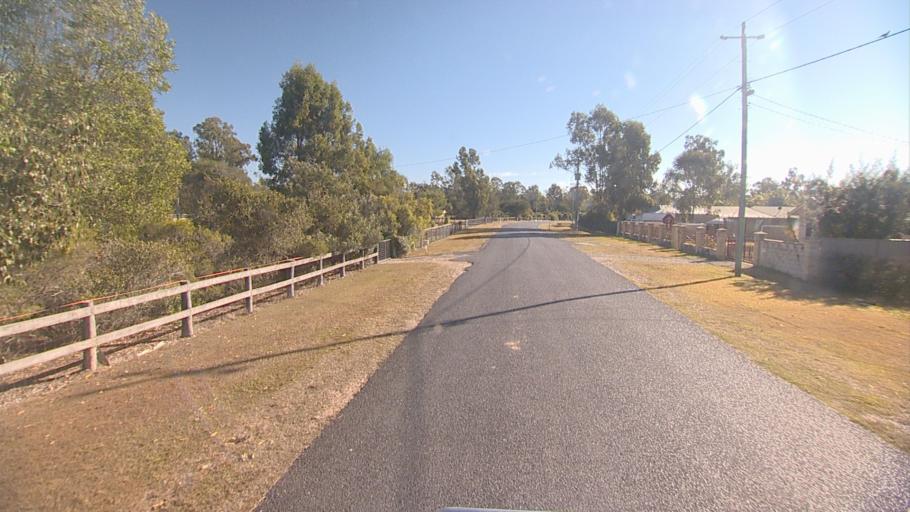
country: AU
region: Queensland
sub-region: Logan
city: North Maclean
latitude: -27.8054
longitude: 152.9785
